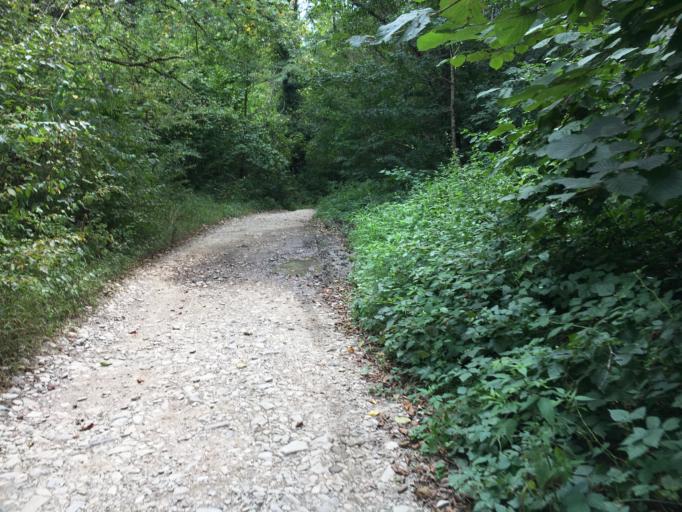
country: RU
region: Krasnodarskiy
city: Tuapse
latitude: 44.2602
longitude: 39.2170
